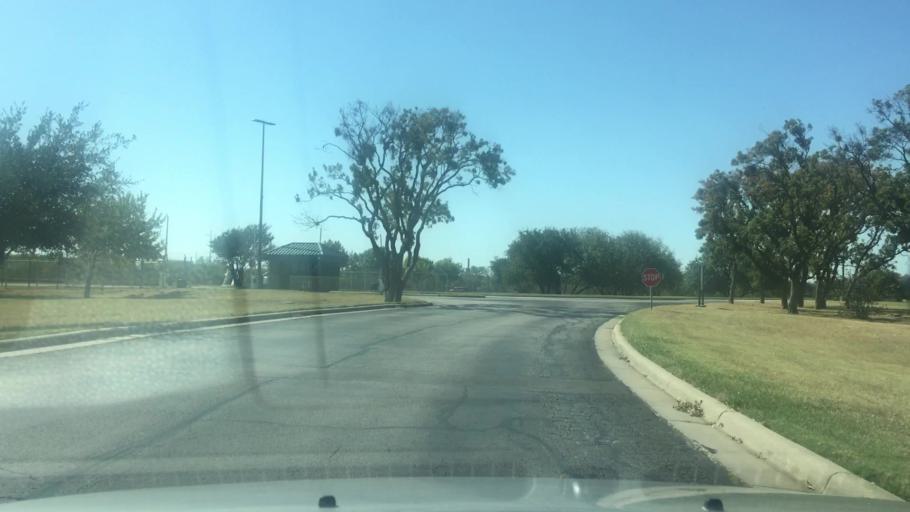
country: US
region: Texas
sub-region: Denton County
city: Denton
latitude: 33.2511
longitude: -97.1512
